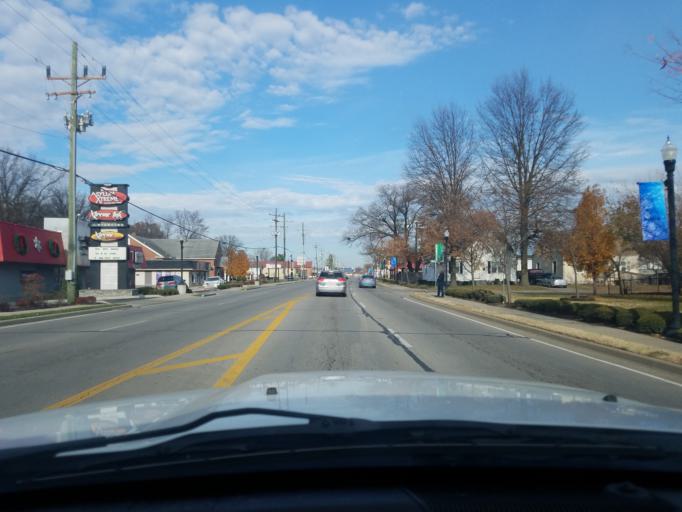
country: US
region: Indiana
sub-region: Clark County
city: Clarksville
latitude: 38.2973
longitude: -85.7603
